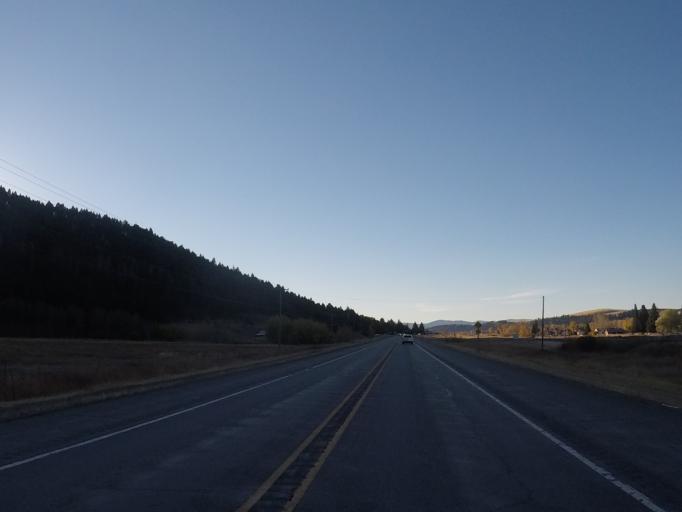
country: US
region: Montana
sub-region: Lewis and Clark County
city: Helena West Side
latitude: 46.5576
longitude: -112.4183
